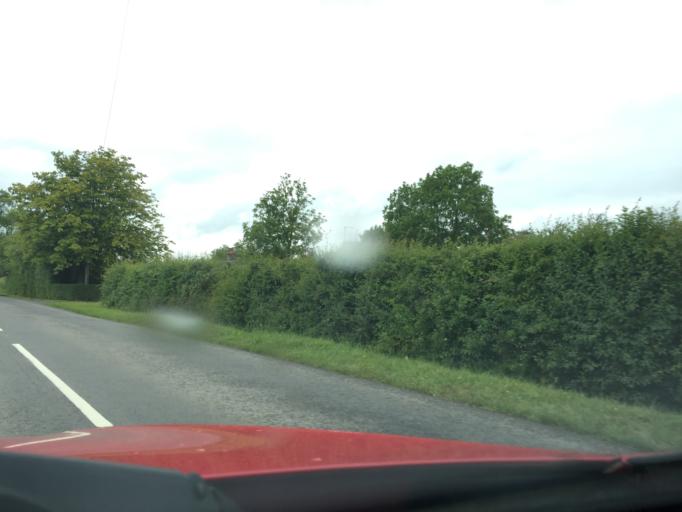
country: GB
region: England
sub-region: Warwickshire
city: Shipston on Stour
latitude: 52.1018
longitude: -1.6371
